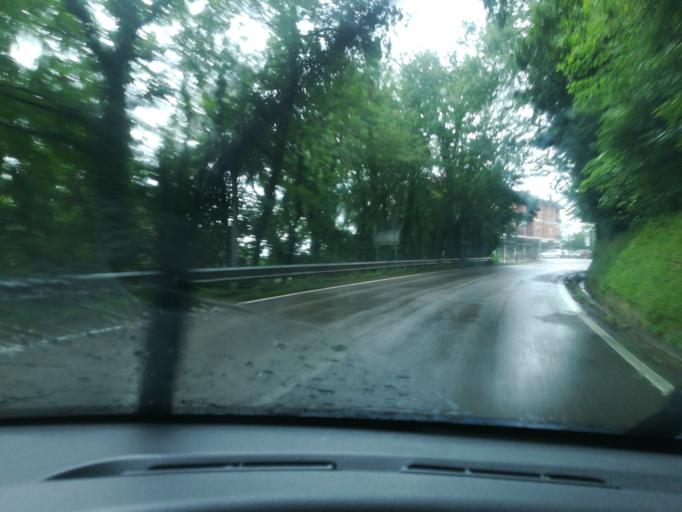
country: IT
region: The Marches
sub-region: Provincia di Macerata
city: Sarnano
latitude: 43.0387
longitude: 13.2954
